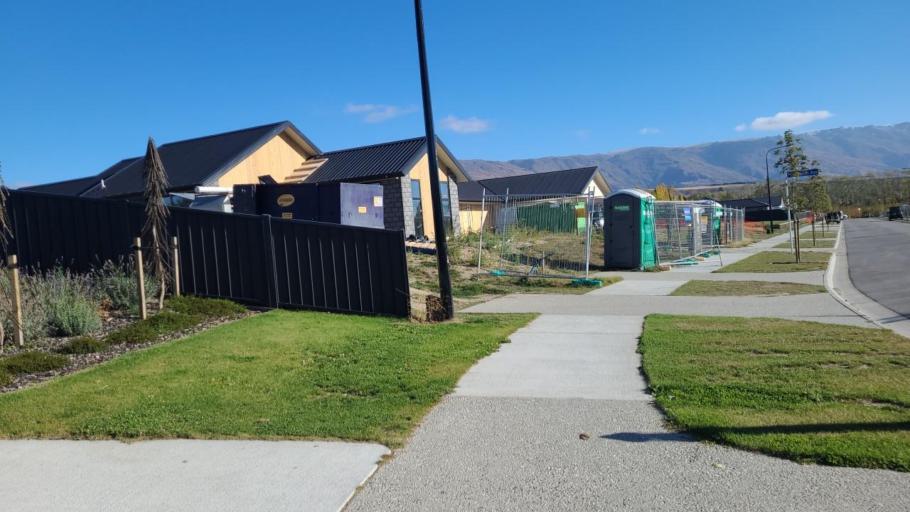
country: NZ
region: Otago
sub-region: Queenstown-Lakes District
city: Wanaka
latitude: -45.0395
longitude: 169.2109
